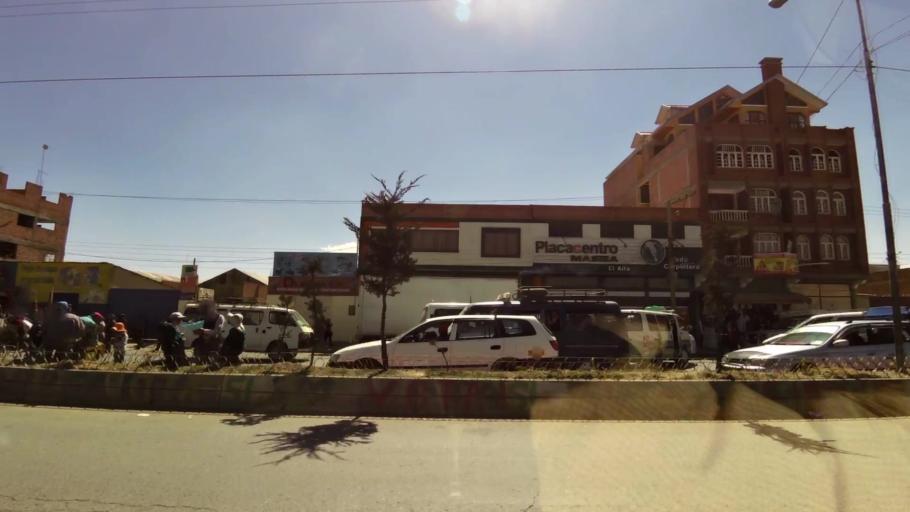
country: BO
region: La Paz
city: La Paz
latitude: -16.4966
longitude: -68.1873
